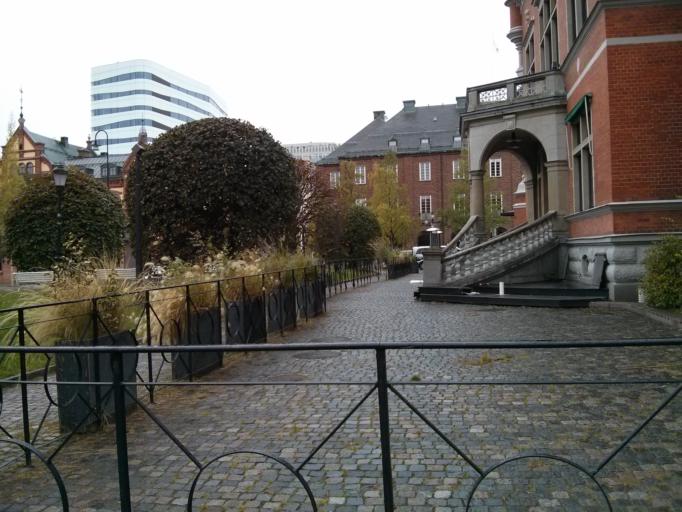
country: SE
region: Vaesterbotten
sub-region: Umea Kommun
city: Umea
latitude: 63.8252
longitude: 20.2631
